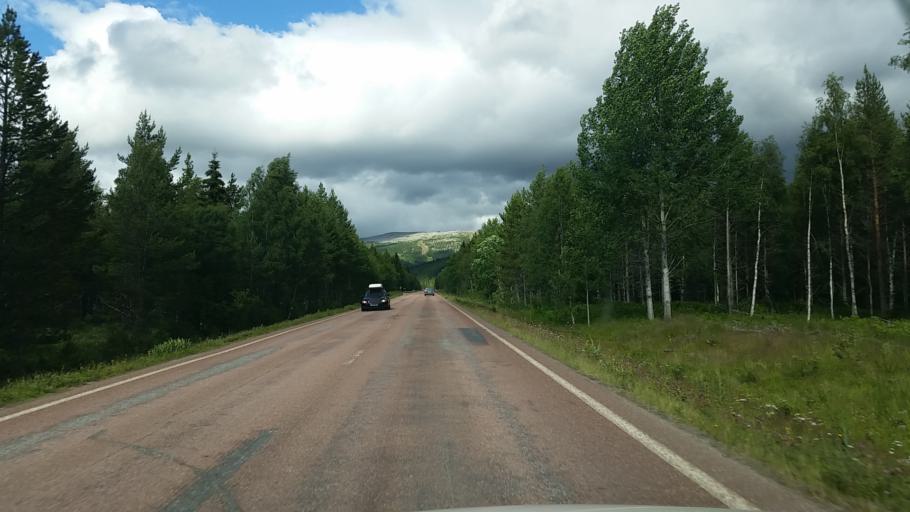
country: SE
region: Jaemtland
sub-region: Harjedalens Kommun
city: Sveg
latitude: 62.4727
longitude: 13.8807
